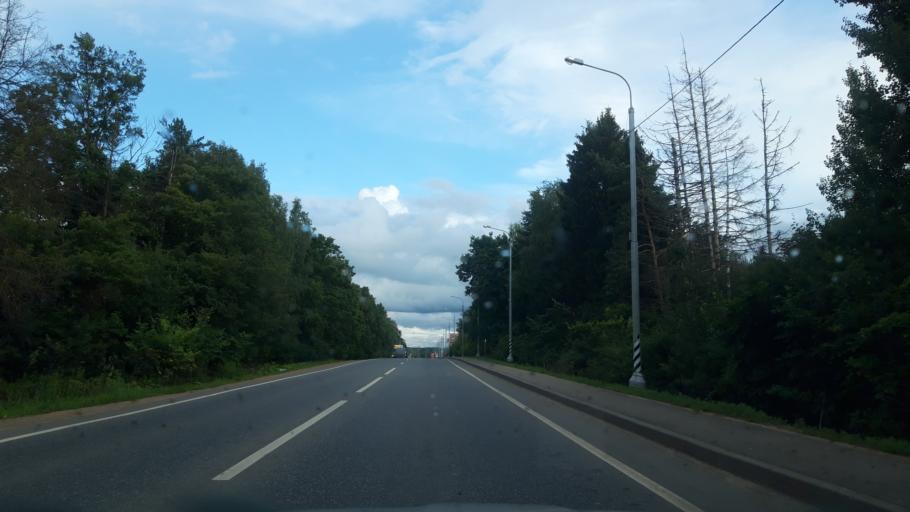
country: RU
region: Moskovskaya
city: Solnechnogorsk
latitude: 56.1276
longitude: 36.9275
